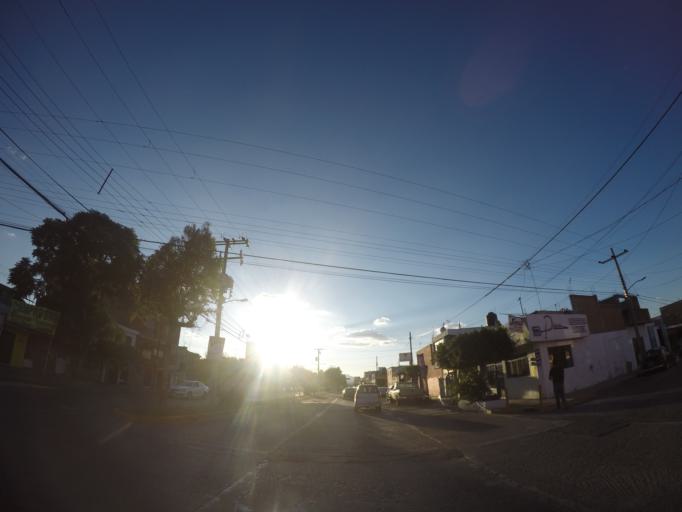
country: MX
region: San Luis Potosi
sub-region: San Luis Potosi
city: San Luis Potosi
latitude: 22.1338
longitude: -100.9758
